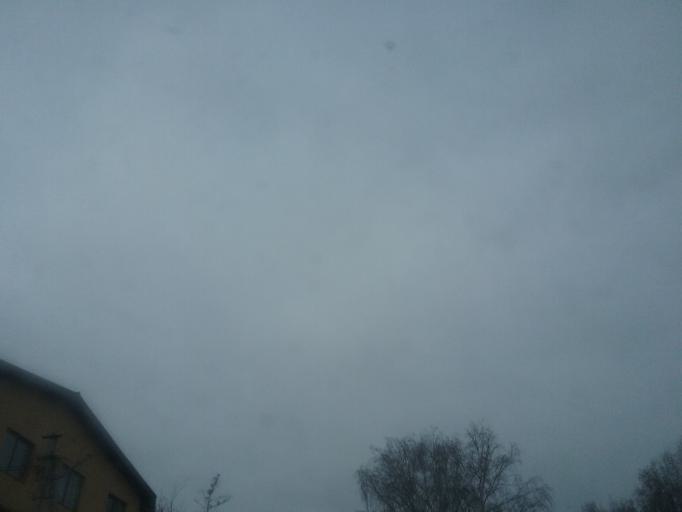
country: RU
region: Tula
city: Tula
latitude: 54.1664
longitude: 37.6214
